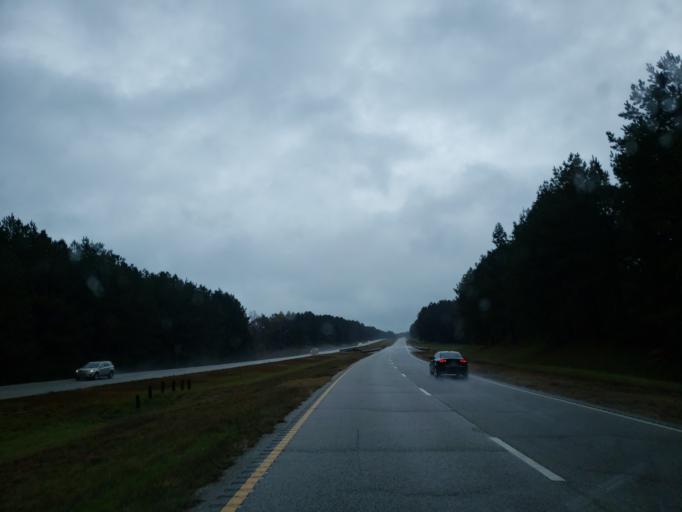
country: US
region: Mississippi
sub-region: Lauderdale County
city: Meridian
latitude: 32.2877
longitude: -88.6981
